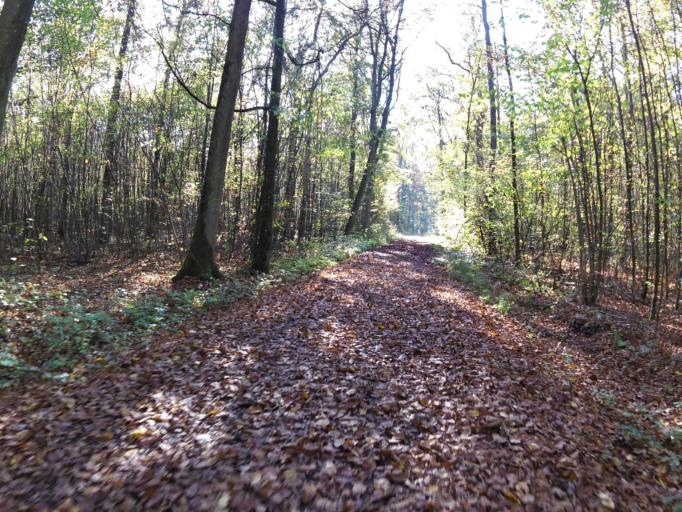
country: DE
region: Bavaria
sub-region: Regierungsbezirk Unterfranken
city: Sulzfeld am Main
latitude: 49.7202
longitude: 10.0897
